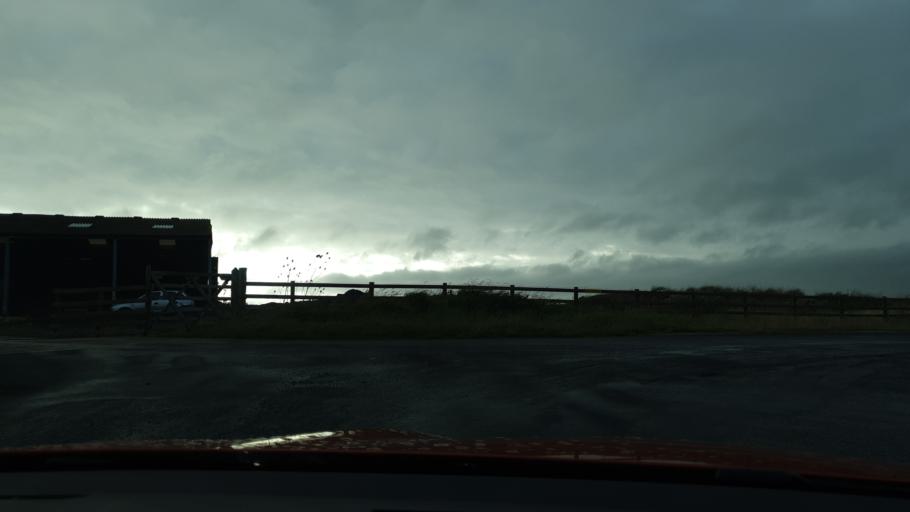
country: GB
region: England
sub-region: Cumbria
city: Barrow in Furness
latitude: 54.0615
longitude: -3.2110
